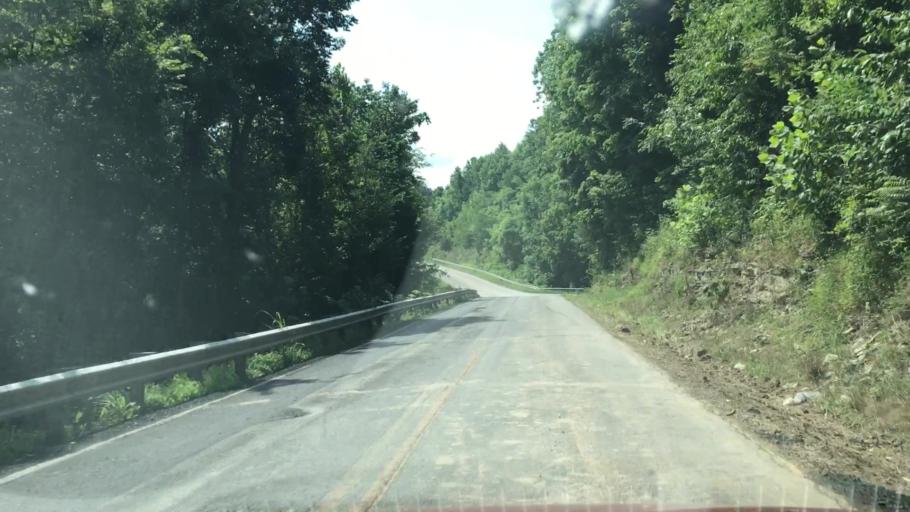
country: US
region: Kentucky
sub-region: Barren County
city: Glasgow
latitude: 36.8609
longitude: -85.8445
